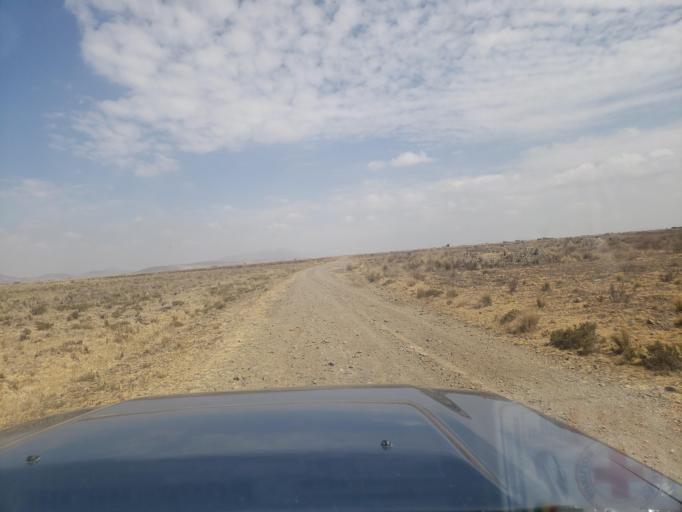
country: BO
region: La Paz
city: Batallas
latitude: -16.4192
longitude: -68.4165
